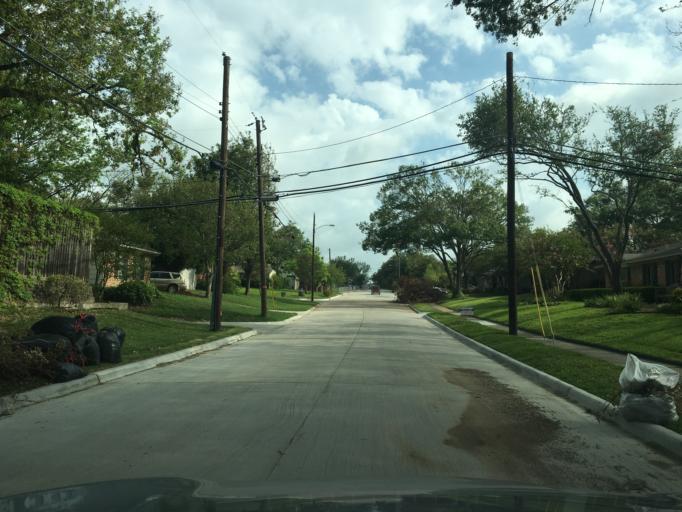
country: US
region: Texas
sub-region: Dallas County
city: Richardson
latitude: 32.9023
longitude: -96.7512
